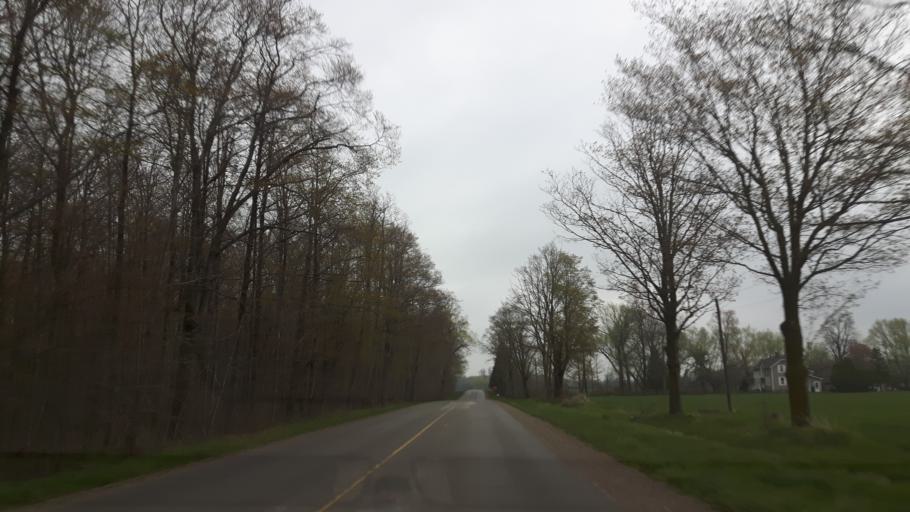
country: CA
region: Ontario
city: Bluewater
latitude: 43.5389
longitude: -81.6743
